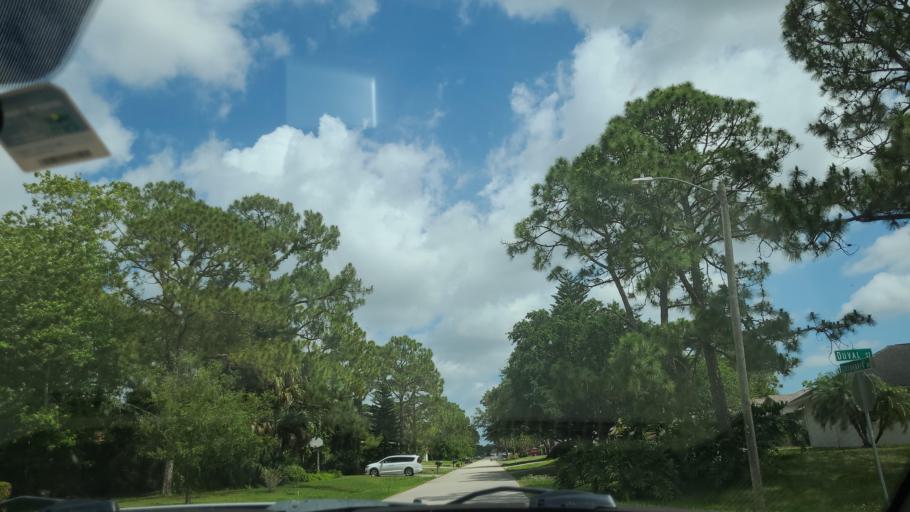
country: US
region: Florida
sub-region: Brevard County
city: West Melbourne
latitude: 28.0000
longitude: -80.6573
